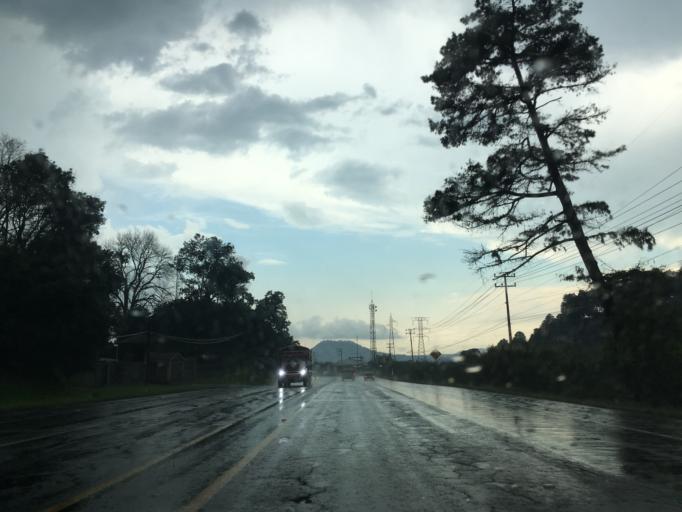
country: MX
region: Michoacan
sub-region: Uruapan
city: Uruapan
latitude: 19.4453
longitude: -102.0766
